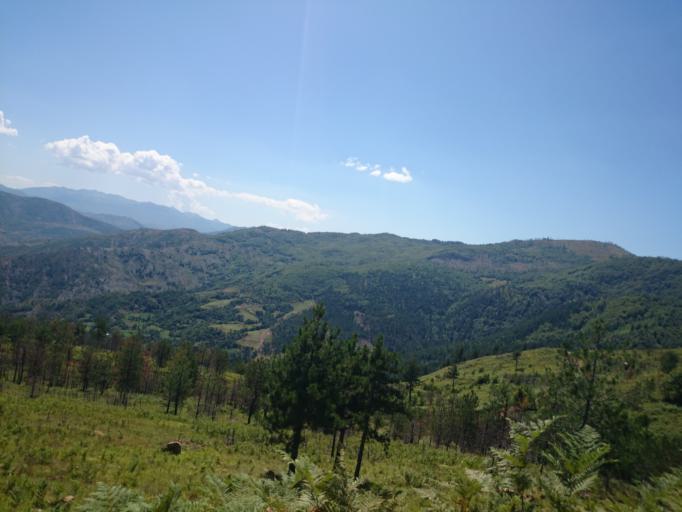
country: AL
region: Diber
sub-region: Rrethi i Bulqizes
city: Zerqan
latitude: 41.4435
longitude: 20.3453
